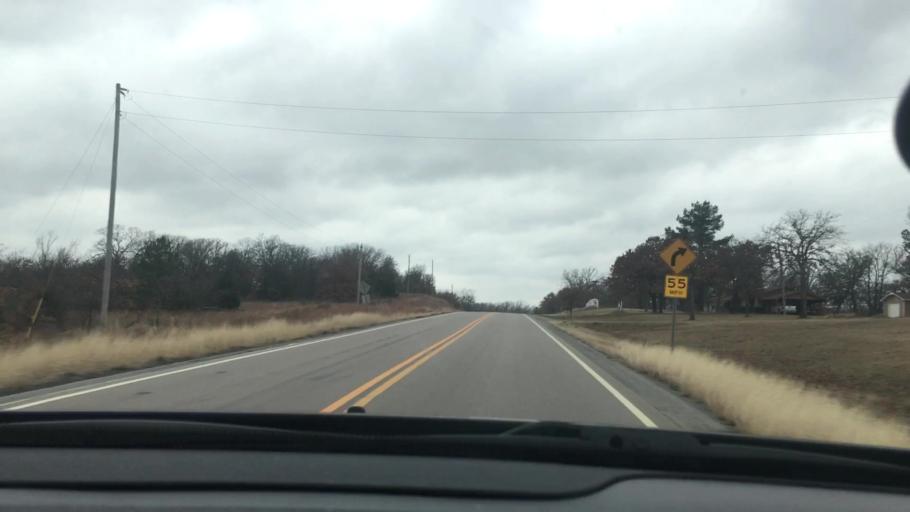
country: US
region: Oklahoma
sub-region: Coal County
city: Coalgate
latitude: 34.3722
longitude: -96.3749
